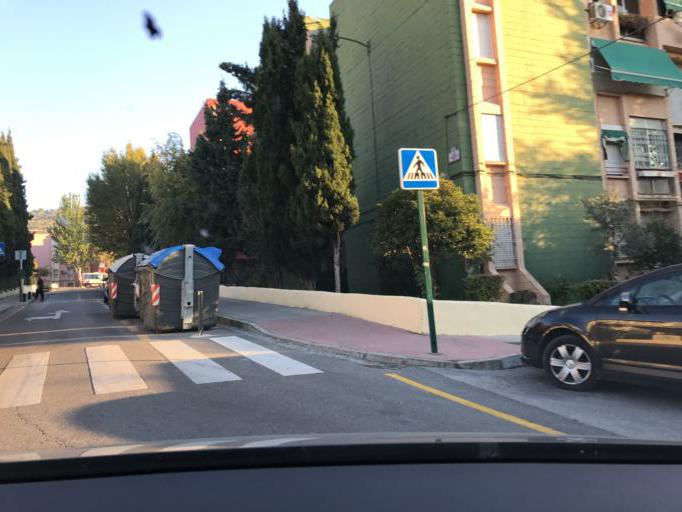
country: ES
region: Andalusia
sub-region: Provincia de Granada
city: Granada
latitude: 37.1995
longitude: -3.5984
